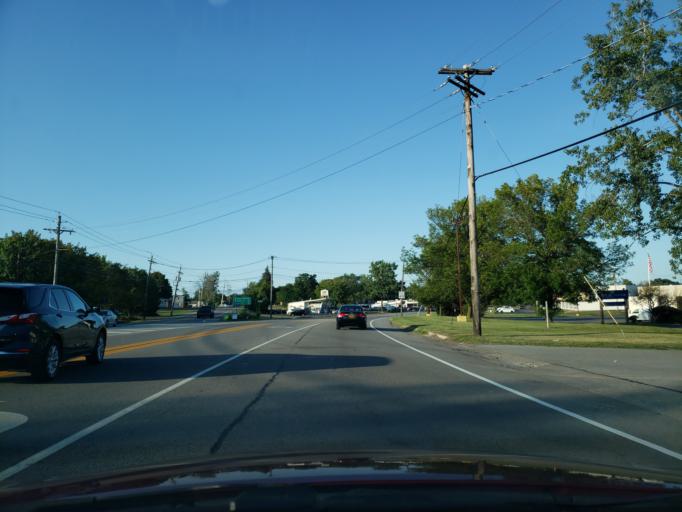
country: US
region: New York
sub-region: Monroe County
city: Webster
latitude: 43.2004
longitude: -77.4983
